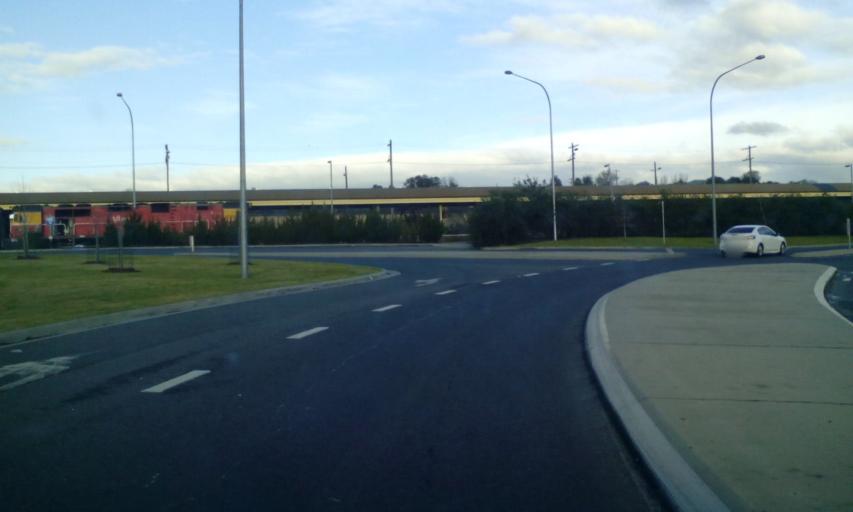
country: AU
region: New South Wales
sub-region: Albury Municipality
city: East Albury
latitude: -36.0859
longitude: 146.9233
